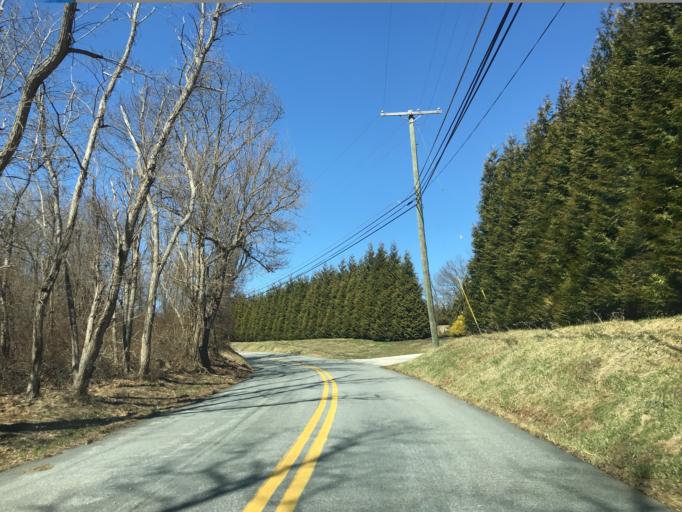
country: US
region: Pennsylvania
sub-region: York County
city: New Freedom
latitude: 39.6823
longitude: -76.6835
